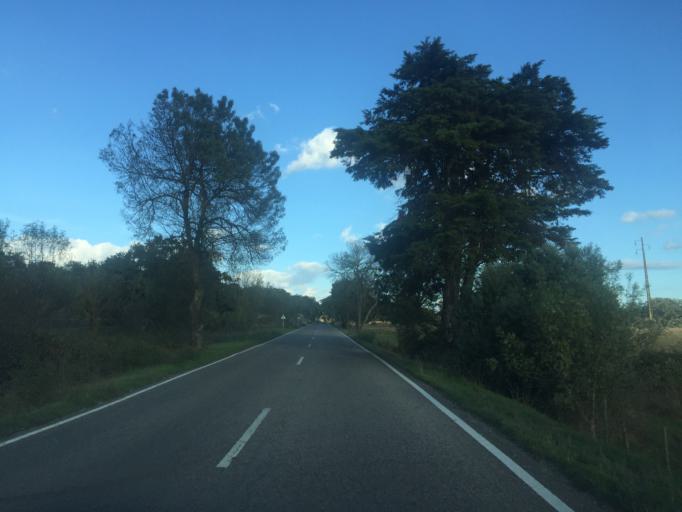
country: PT
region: Portalegre
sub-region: Alter do Chao
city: Alter do Chao
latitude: 39.1958
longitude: -7.6845
